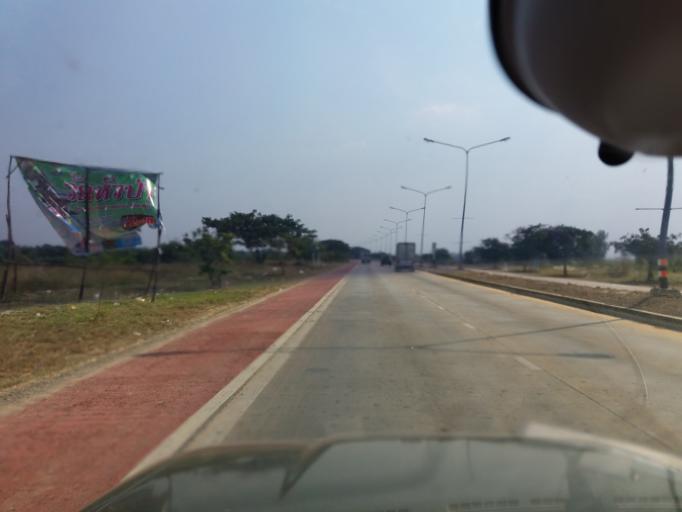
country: TH
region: Sing Buri
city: Sing Buri
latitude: 14.8813
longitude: 100.3923
